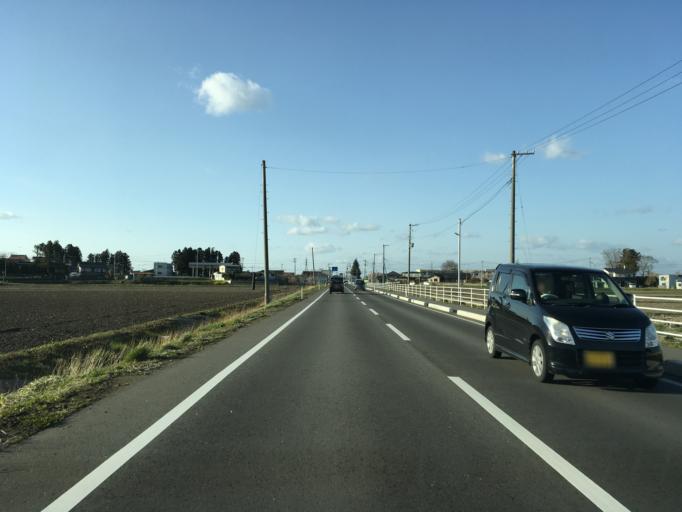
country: JP
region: Miyagi
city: Wakuya
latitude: 38.6577
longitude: 141.1930
